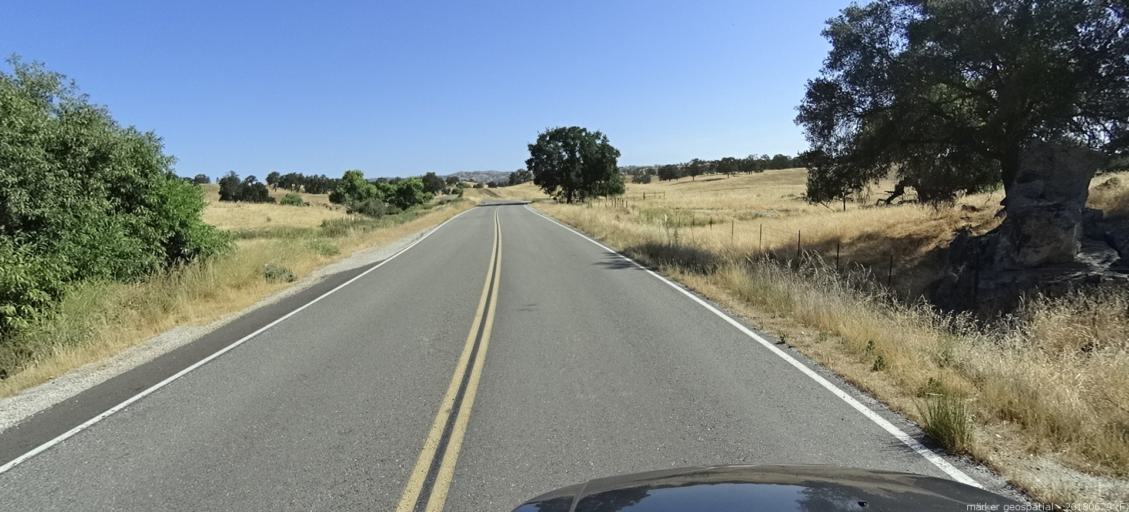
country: US
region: California
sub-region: Madera County
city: Bonadelle Ranchos-Madera Ranchos
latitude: 37.0529
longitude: -119.7935
